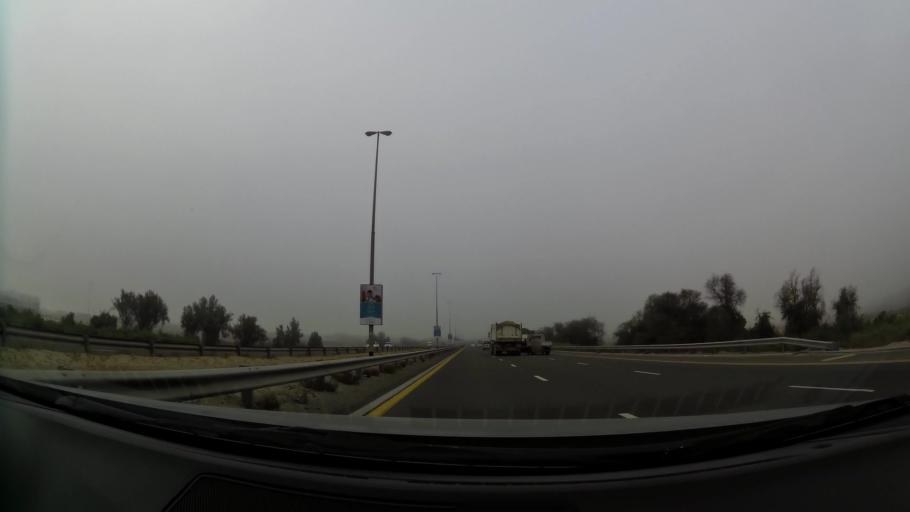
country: AE
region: Dubai
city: Dubai
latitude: 25.1443
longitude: 55.3445
